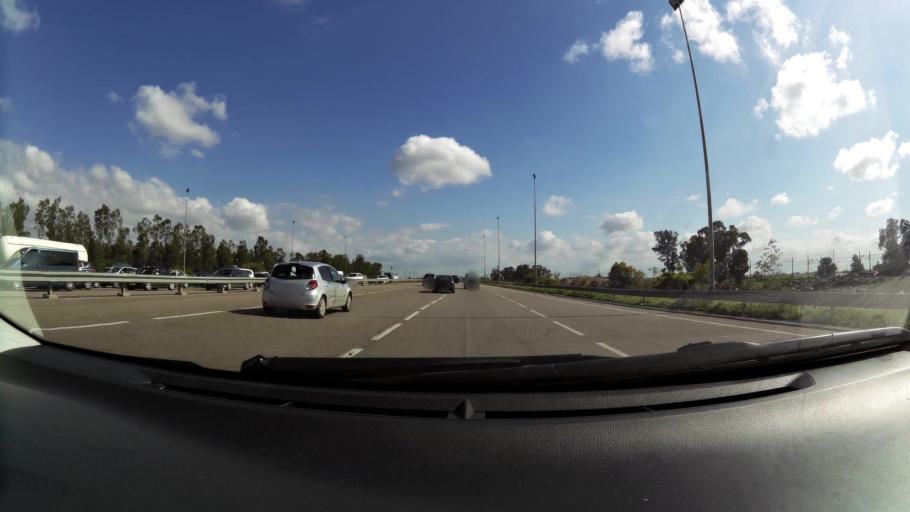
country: MA
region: Chaouia-Ouardigha
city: Nouaseur
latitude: 33.3655
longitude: -7.6201
